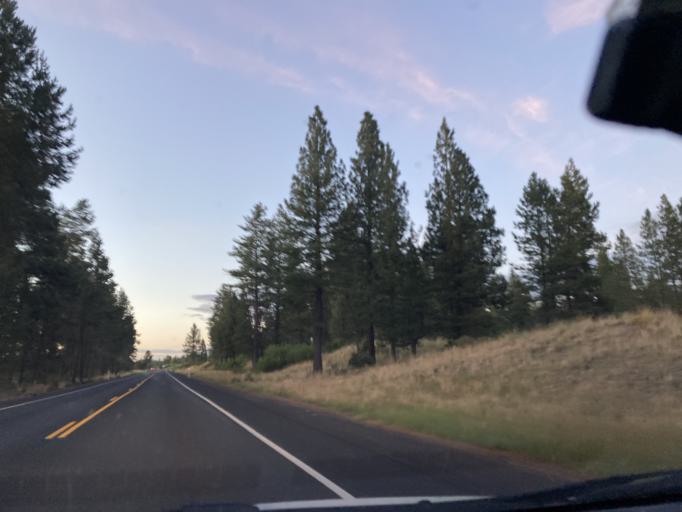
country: US
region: Oregon
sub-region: Deschutes County
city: Three Rivers
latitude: 43.8458
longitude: -121.4412
